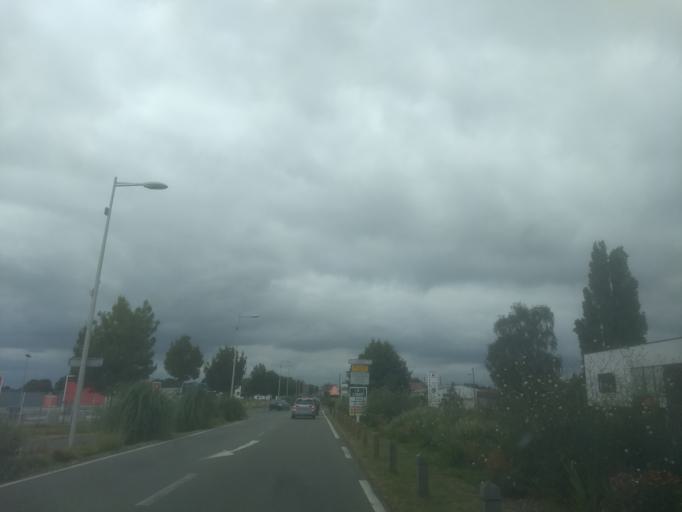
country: FR
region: Nord-Pas-de-Calais
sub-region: Departement du Pas-de-Calais
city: Carvin
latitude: 50.4809
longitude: 2.9650
